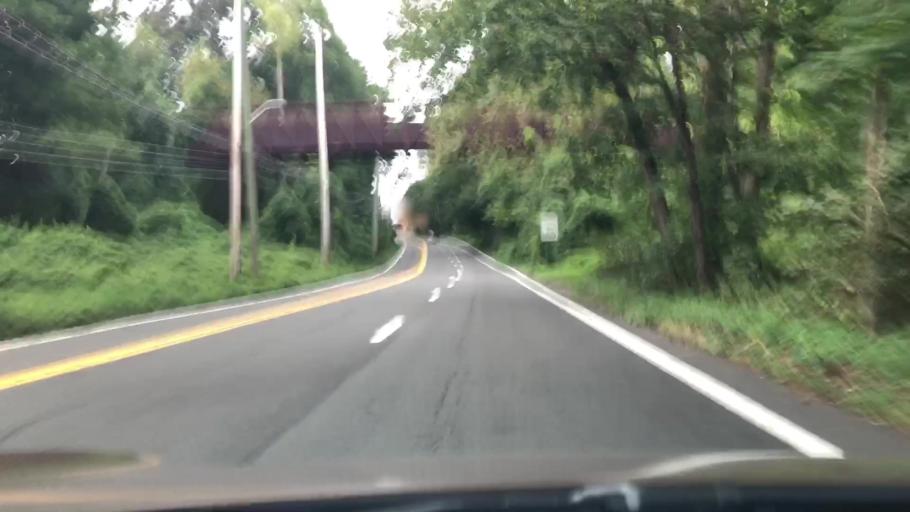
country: US
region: New York
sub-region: Westchester County
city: Sleepy Hollow
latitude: 41.1186
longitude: -73.8605
